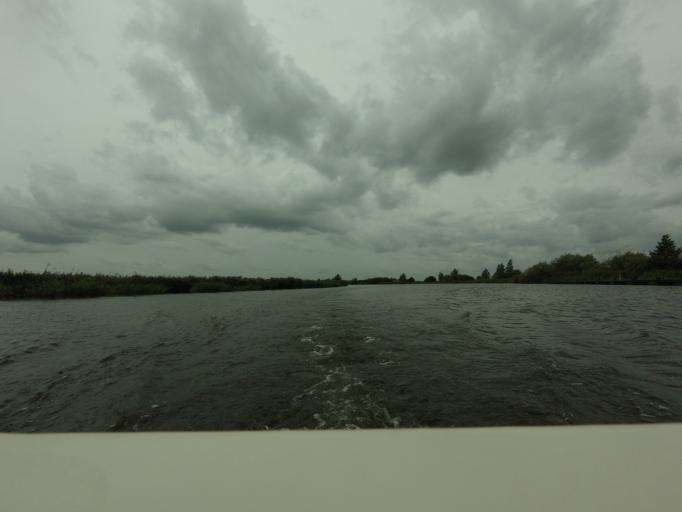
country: NL
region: Friesland
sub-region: Gemeente Boarnsterhim
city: Aldeboarn
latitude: 53.0994
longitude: 5.9170
